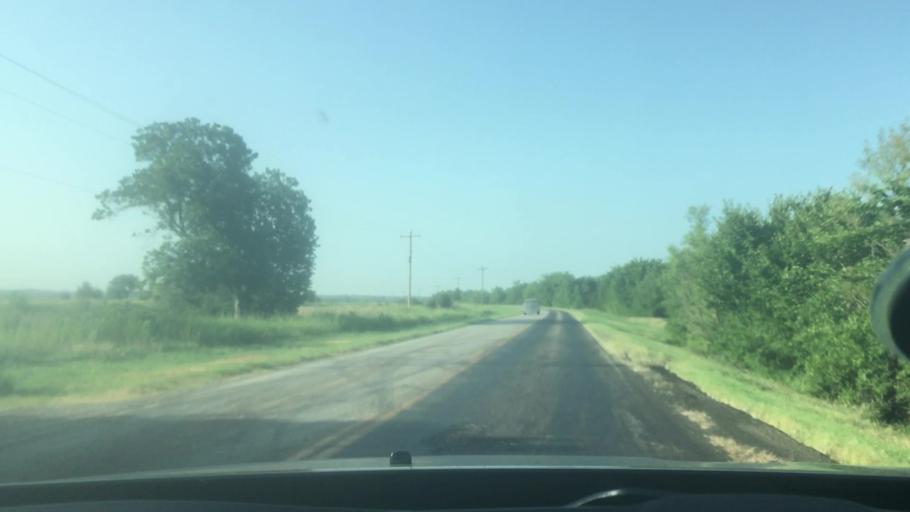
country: US
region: Oklahoma
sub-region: Coal County
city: Coalgate
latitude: 34.3532
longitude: -96.4246
